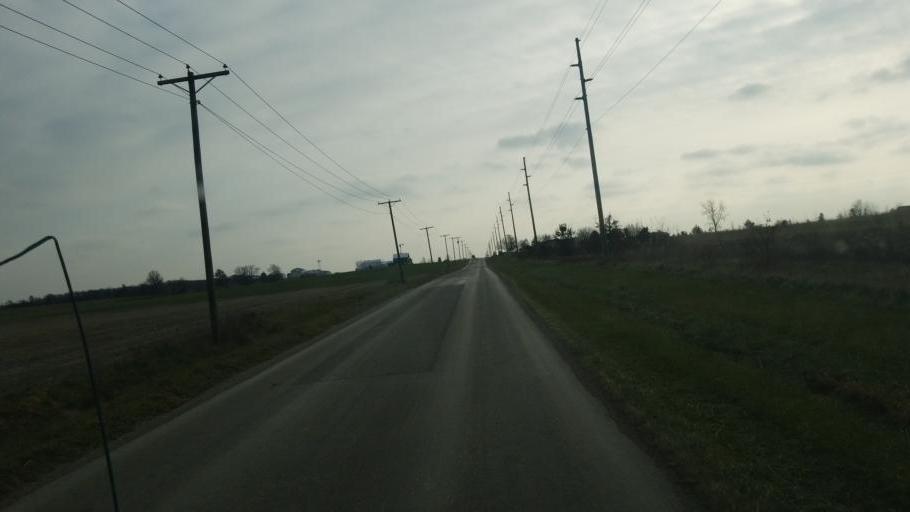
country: US
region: Indiana
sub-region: Adams County
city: Berne
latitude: 40.6388
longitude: -84.9643
